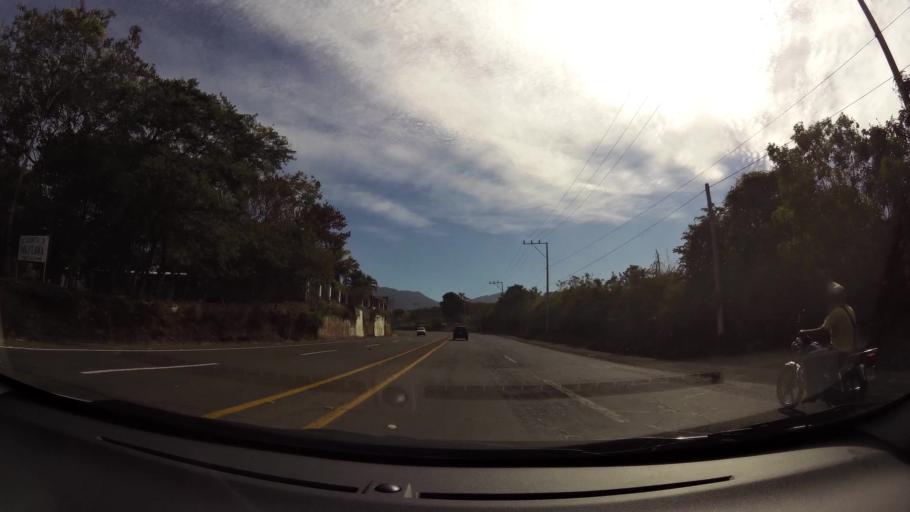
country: SV
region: Santa Ana
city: Chalchuapa
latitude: 13.9864
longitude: -89.6907
